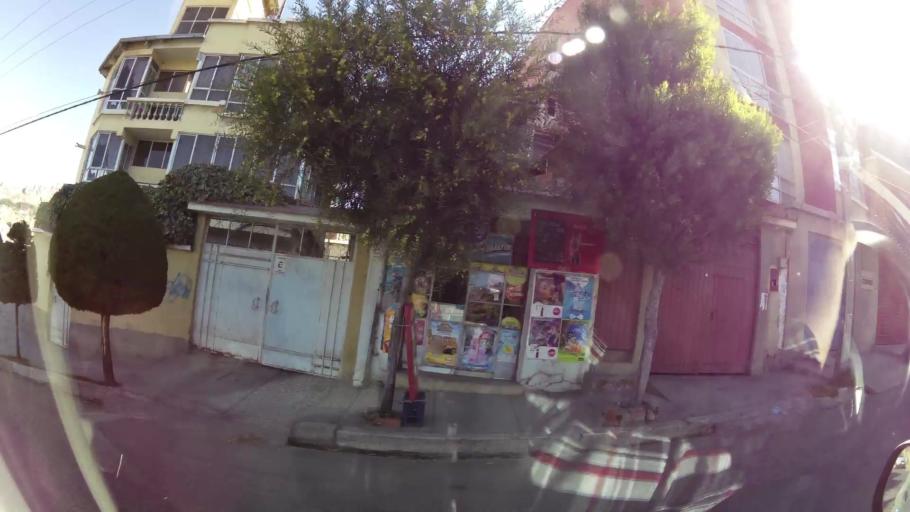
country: BO
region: La Paz
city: La Paz
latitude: -16.5192
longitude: -68.1277
